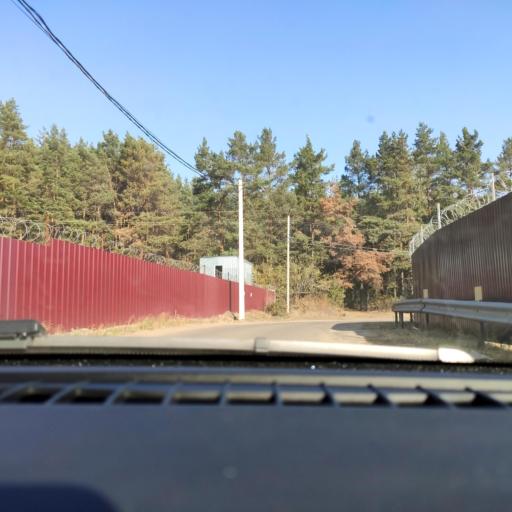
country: RU
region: Voronezj
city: Maslovka
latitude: 51.5455
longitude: 39.2190
